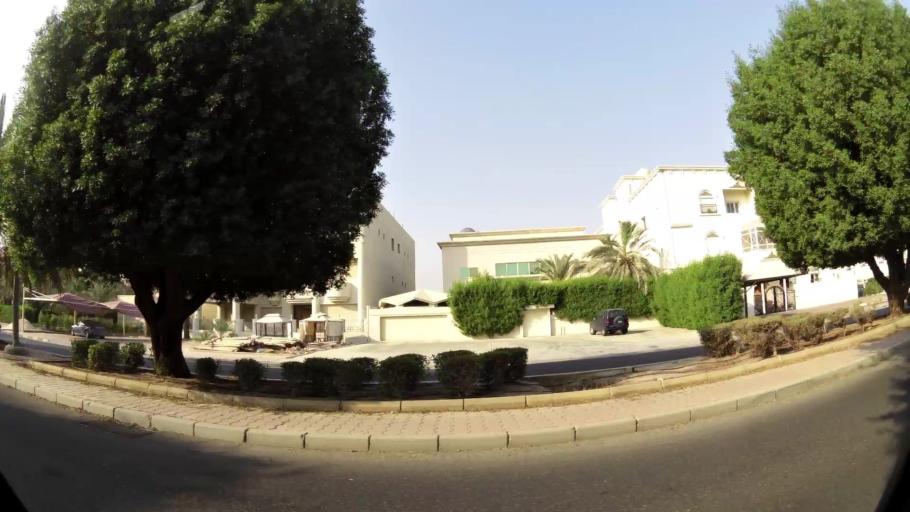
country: KW
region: Muhafazat Hawalli
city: Salwa
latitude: 29.2777
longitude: 48.0790
